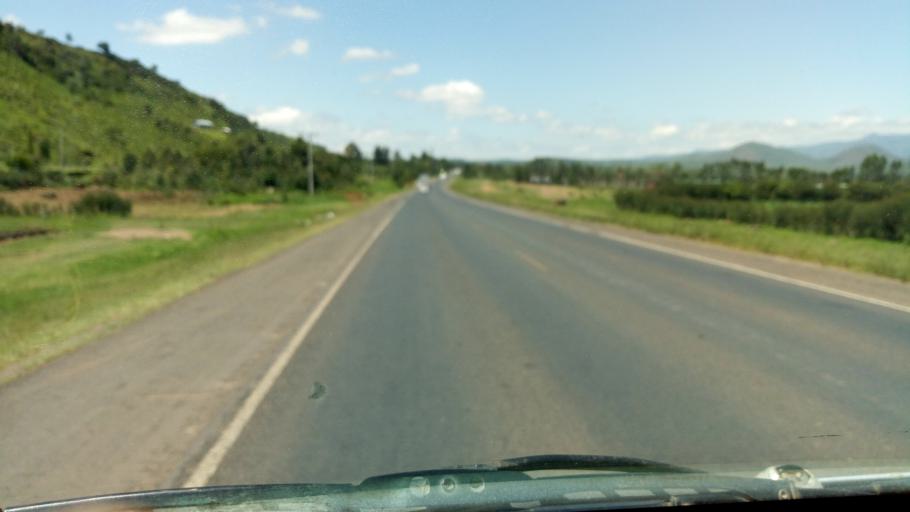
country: KE
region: Nyandarua
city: Ol Kalou
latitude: -0.4369
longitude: 36.2663
